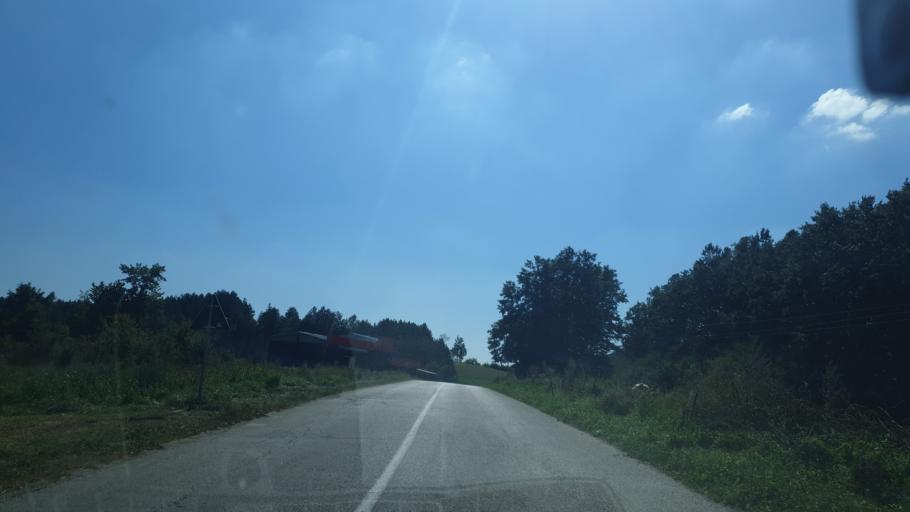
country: RS
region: Central Serbia
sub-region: Zlatiborski Okrug
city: Kosjeric
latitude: 43.9882
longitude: 20.0430
